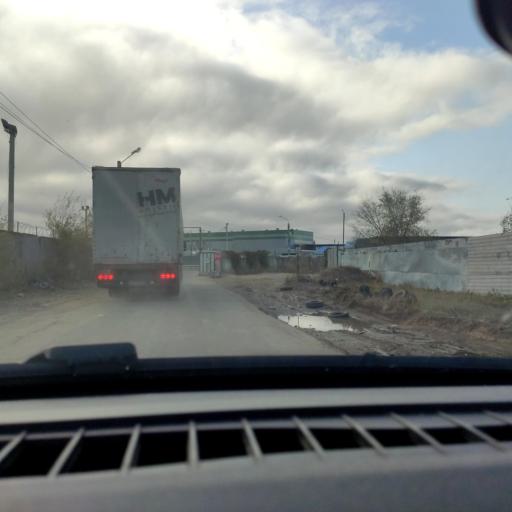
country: RU
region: Voronezj
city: Maslovka
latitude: 51.5972
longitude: 39.2335
